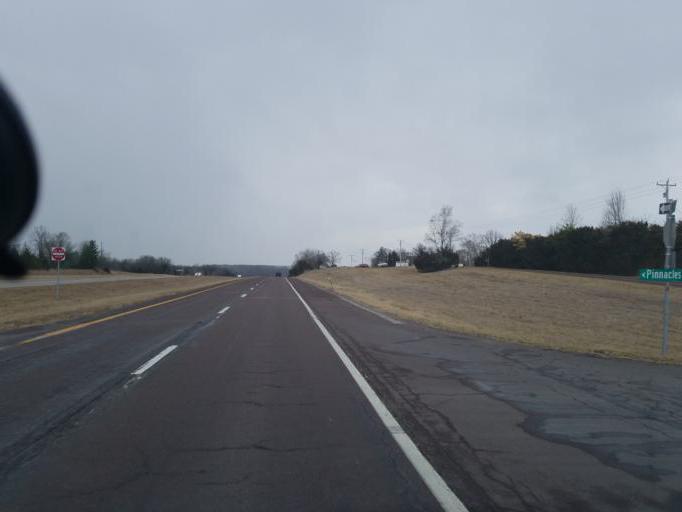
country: US
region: Missouri
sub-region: Boone County
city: Hallsville
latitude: 39.1387
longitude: -92.3325
